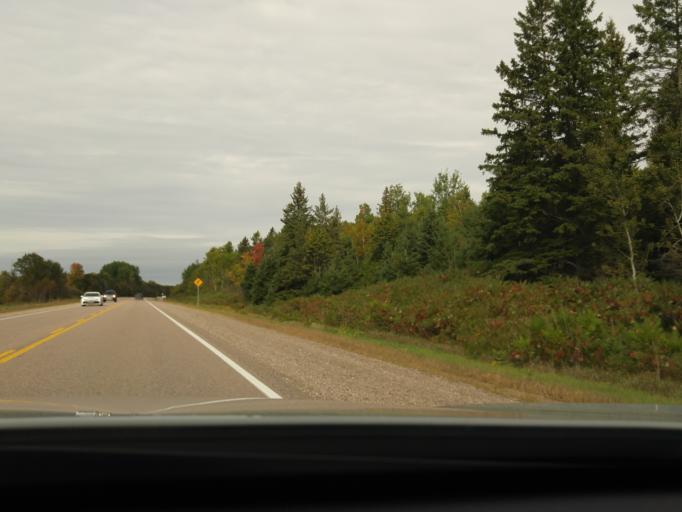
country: CA
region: Ontario
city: Renfrew
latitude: 45.5554
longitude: -76.7404
